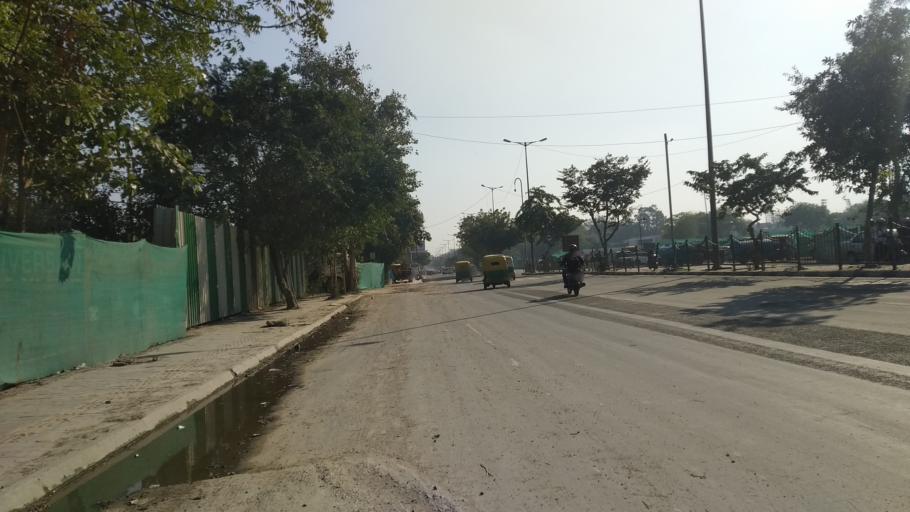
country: IN
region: NCT
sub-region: New Delhi
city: New Delhi
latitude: 28.6175
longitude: 77.2404
